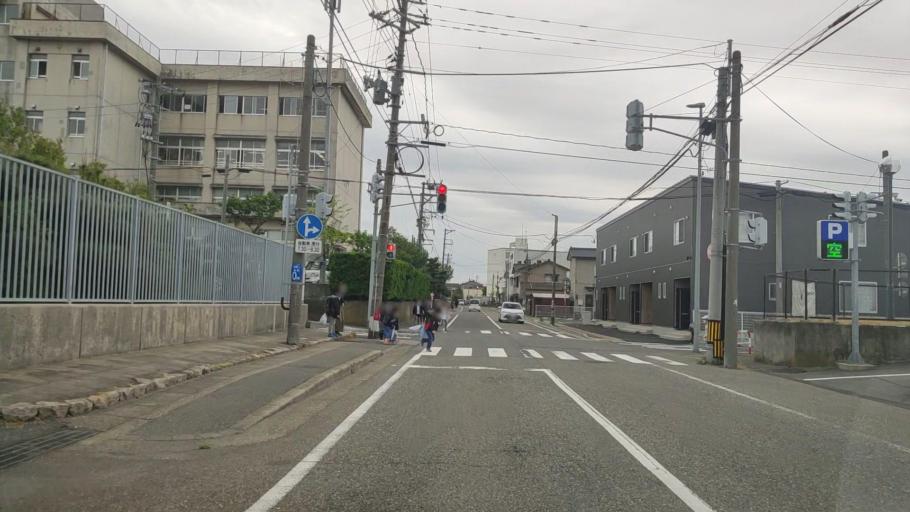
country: JP
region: Niigata
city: Niigata-shi
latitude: 37.9448
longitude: 139.0776
